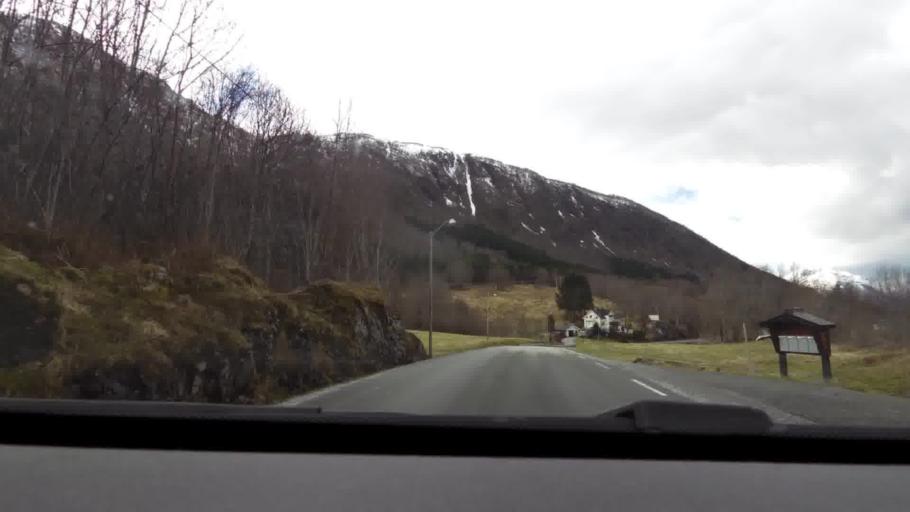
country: NO
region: More og Romsdal
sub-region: Eide
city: Eide
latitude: 62.9068
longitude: 7.5261
